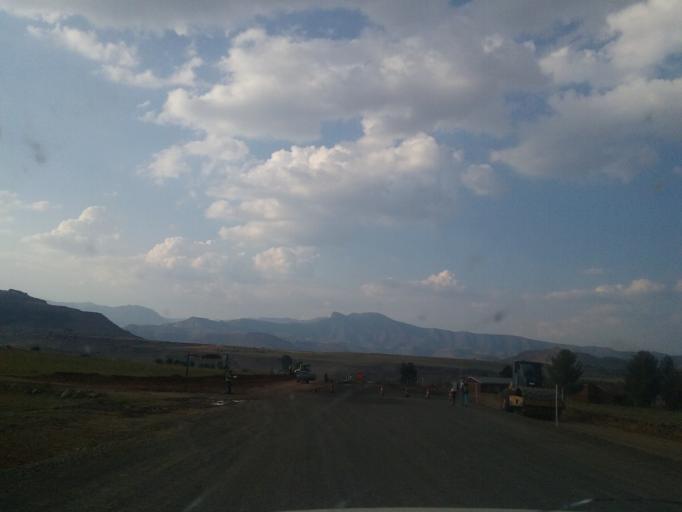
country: LS
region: Quthing
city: Quthing
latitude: -30.3997
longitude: 27.6114
